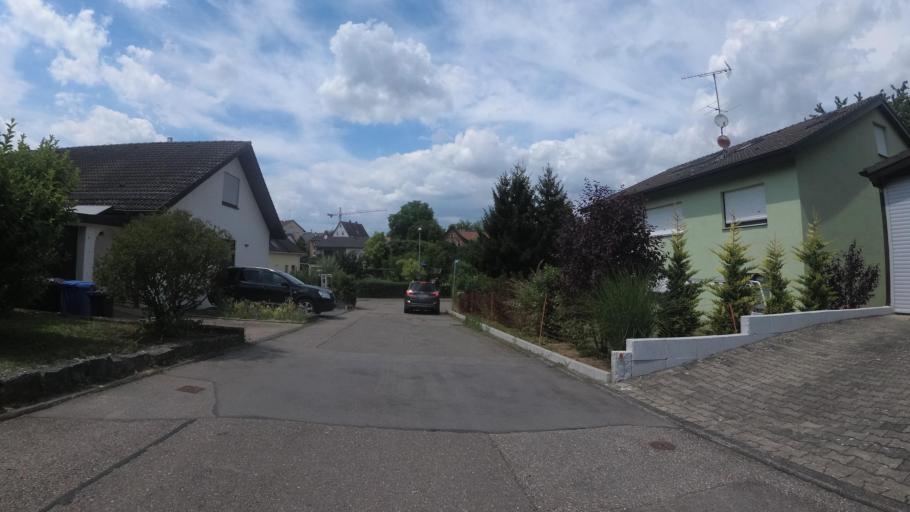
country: DE
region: Baden-Wuerttemberg
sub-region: Regierungsbezirk Stuttgart
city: Neuenstadt am Kocher
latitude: 49.2586
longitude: 9.3024
